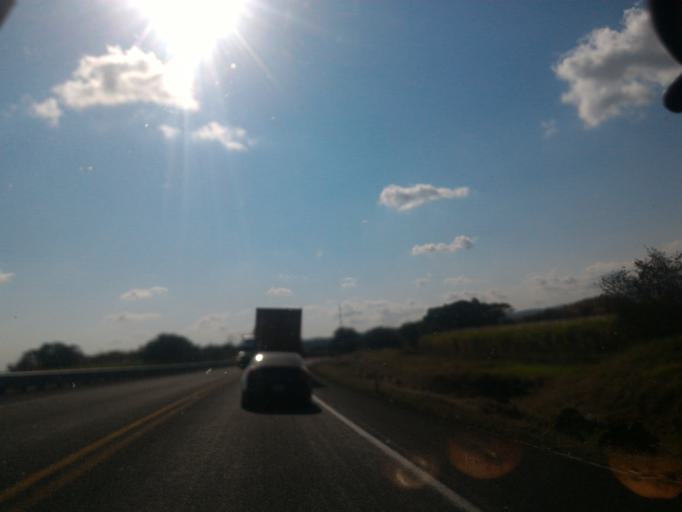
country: MX
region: Jalisco
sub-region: Tonila
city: San Marcos
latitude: 19.4354
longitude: -103.4821
